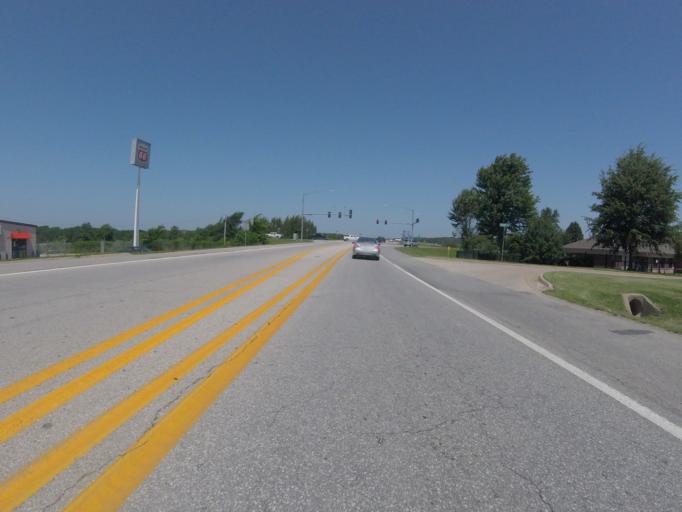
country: US
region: Arkansas
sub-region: Washington County
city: Johnson
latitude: 36.1039
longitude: -94.1785
